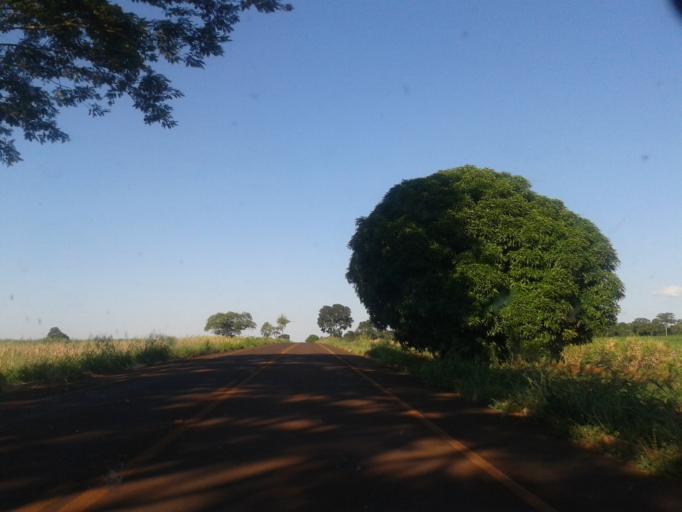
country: BR
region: Minas Gerais
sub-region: Santa Vitoria
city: Santa Vitoria
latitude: -18.6950
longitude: -49.9286
